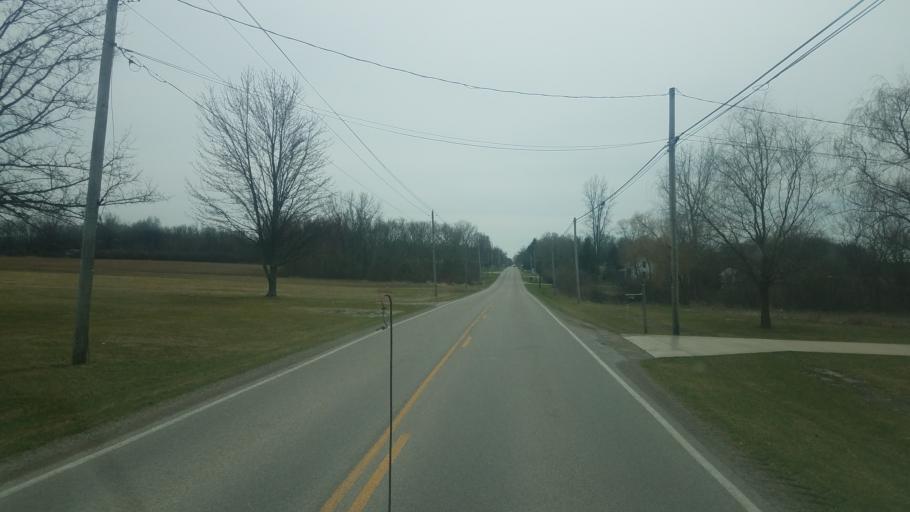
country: US
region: Ohio
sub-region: Huron County
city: Wakeman
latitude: 41.2544
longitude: -82.4916
